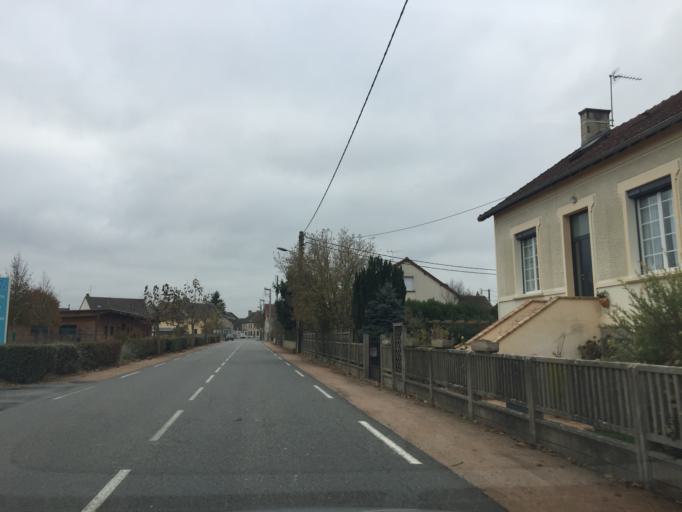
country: FR
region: Limousin
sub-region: Departement de la Creuse
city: Gouzon
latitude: 46.1955
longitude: 2.2389
